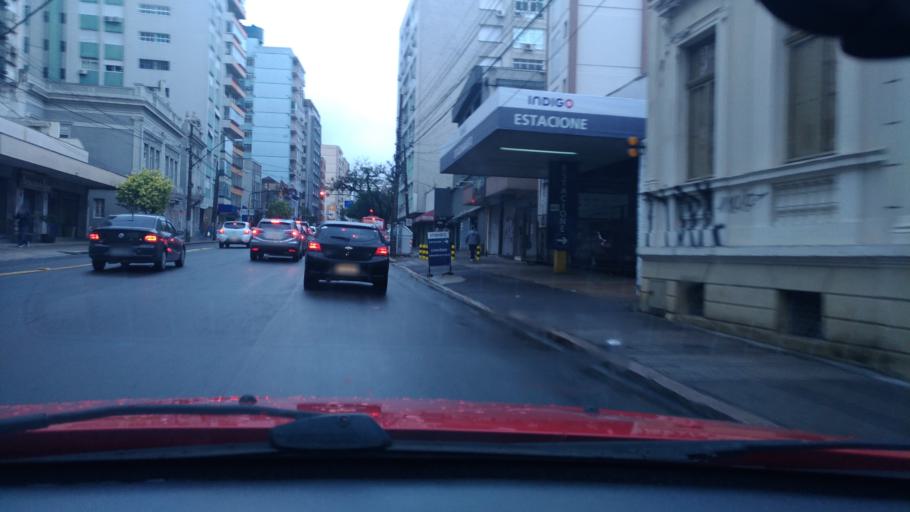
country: BR
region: Rio Grande do Sul
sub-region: Porto Alegre
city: Porto Alegre
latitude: -30.0294
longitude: -51.2169
